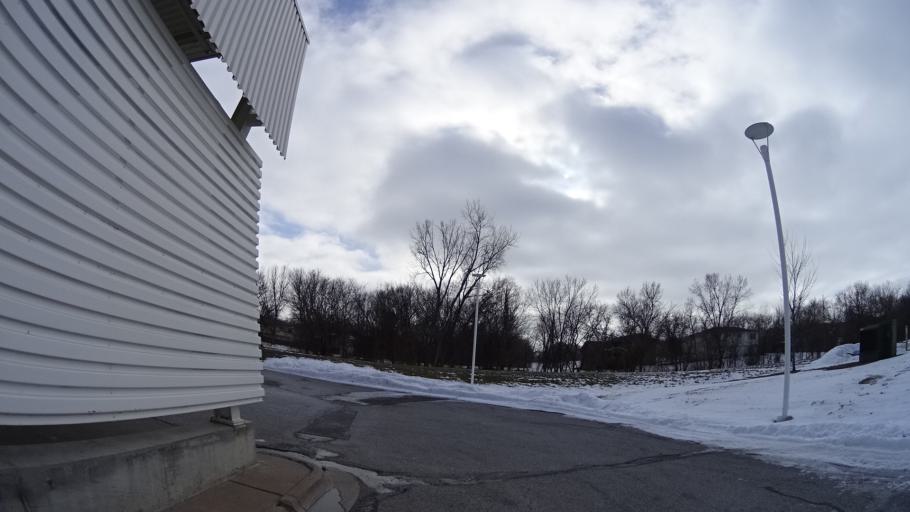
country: US
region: Nebraska
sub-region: Sarpy County
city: Offutt Air Force Base
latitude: 41.1168
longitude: -95.9459
